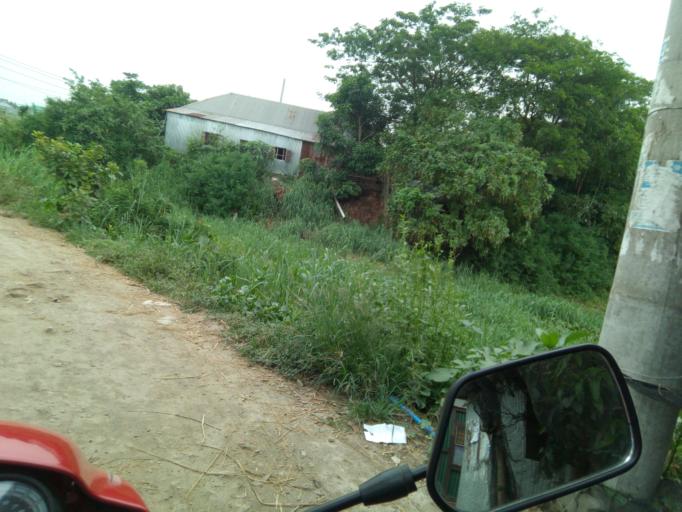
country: BD
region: Dhaka
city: Paltan
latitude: 23.7485
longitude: 90.4617
